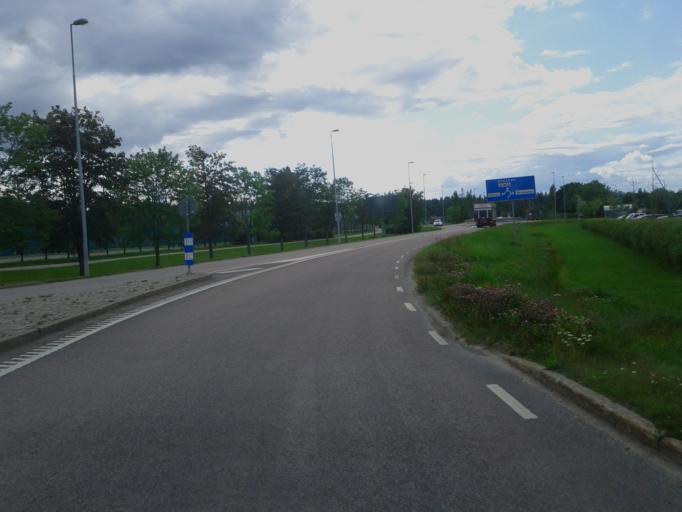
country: SE
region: Vaestmanland
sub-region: Sala Kommun
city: Sala
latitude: 59.9220
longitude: 16.5881
